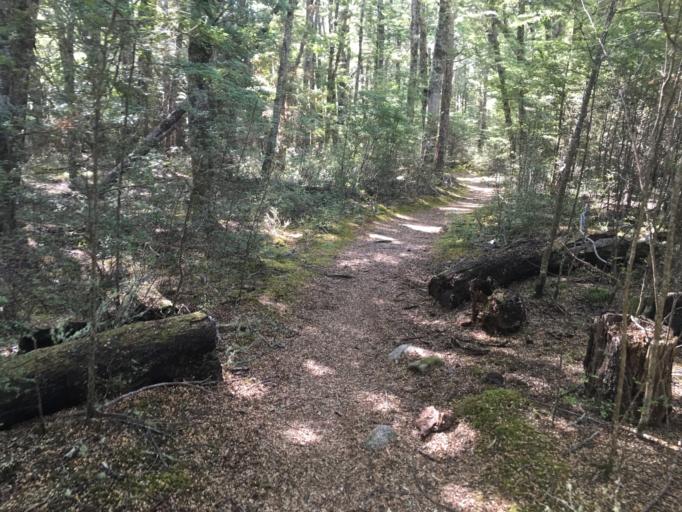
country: NZ
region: Southland
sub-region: Southland District
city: Te Anau
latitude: -45.4849
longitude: 167.6831
